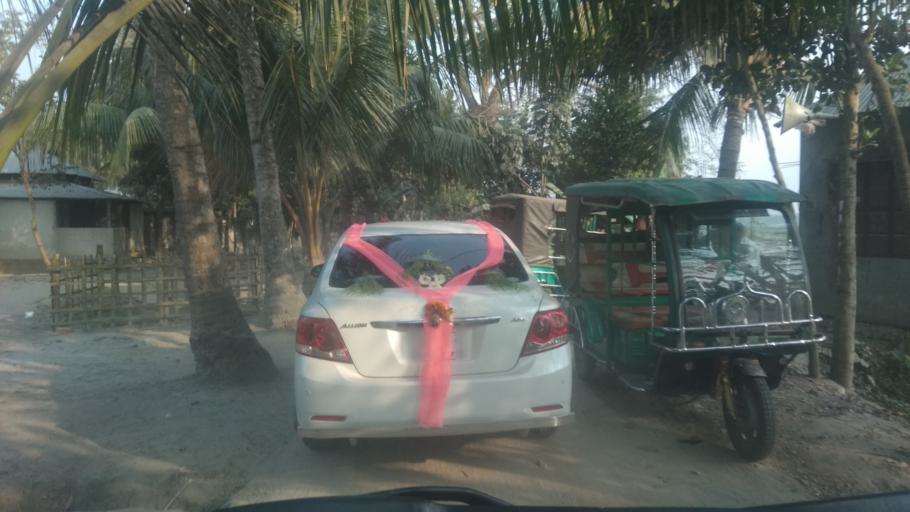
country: BD
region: Dhaka
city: Netrakona
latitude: 24.7749
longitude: 90.6081
